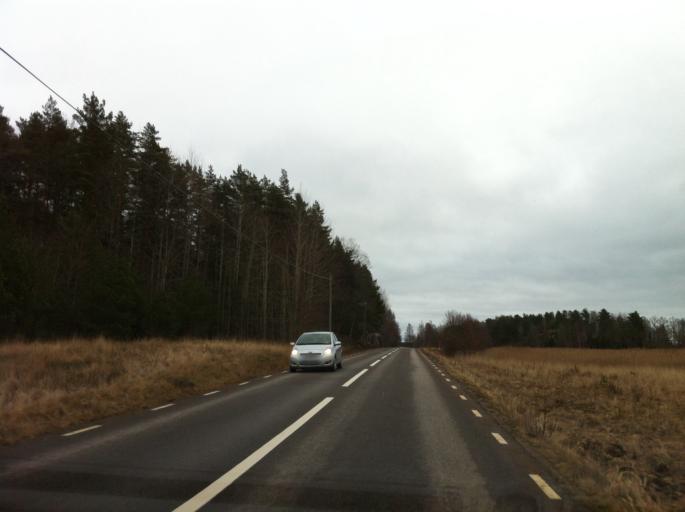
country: SE
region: Kalmar
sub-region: Vasterviks Kommun
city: Overum
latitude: 57.9099
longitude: 16.1802
